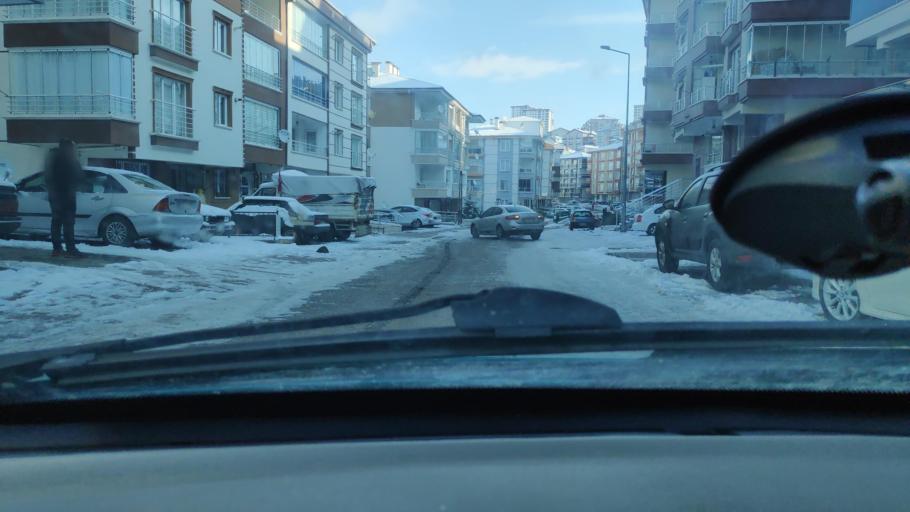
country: TR
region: Ankara
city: Ankara
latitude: 40.0107
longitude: 32.8432
